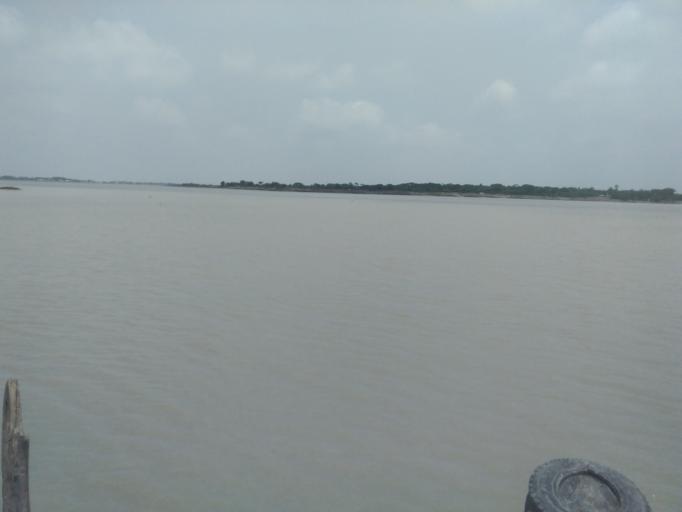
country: BD
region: Khulna
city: Phultala
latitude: 22.6412
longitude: 89.4133
